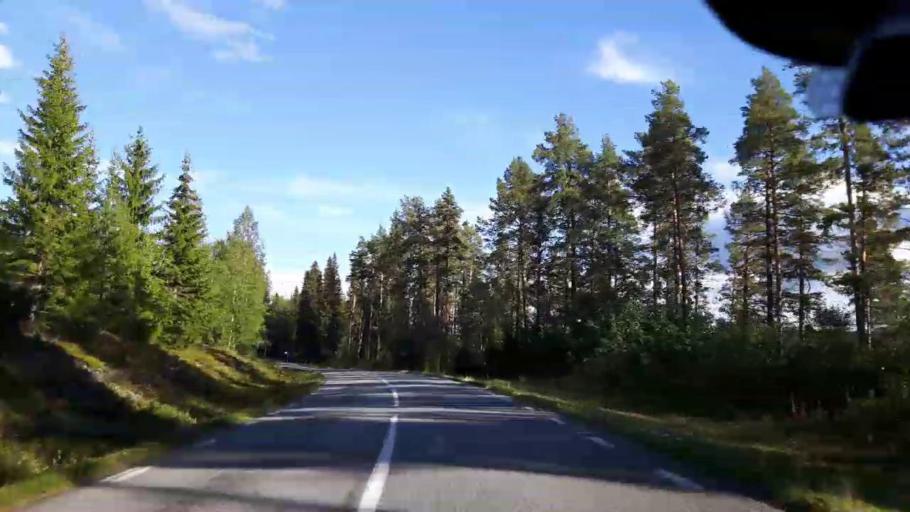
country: SE
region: Jaemtland
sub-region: Stroemsunds Kommun
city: Stroemsund
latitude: 63.3725
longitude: 15.5640
